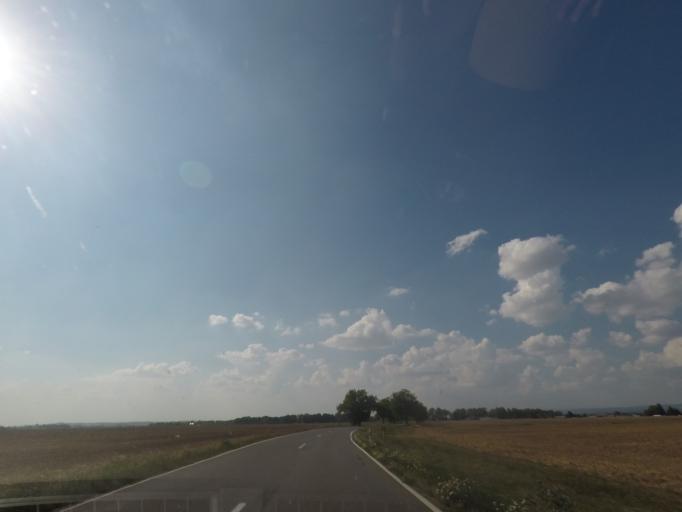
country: CZ
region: Kralovehradecky
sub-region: Okres Nachod
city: Jaromer
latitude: 50.3290
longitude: 15.9449
